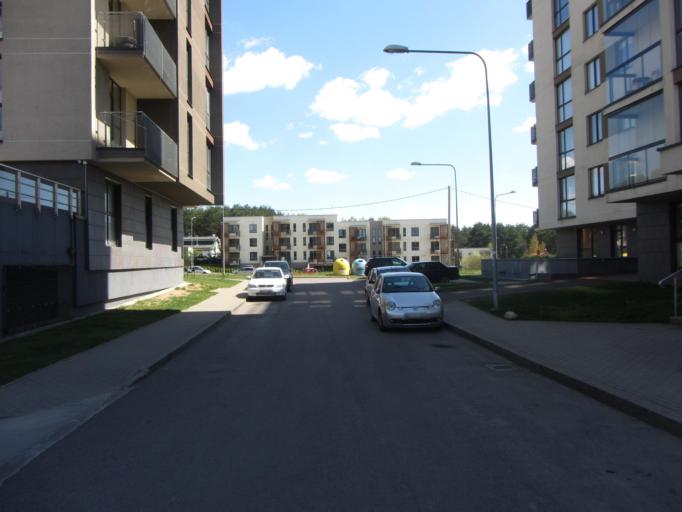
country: LT
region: Vilnius County
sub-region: Vilnius
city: Fabijoniskes
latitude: 54.7551
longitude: 25.2647
